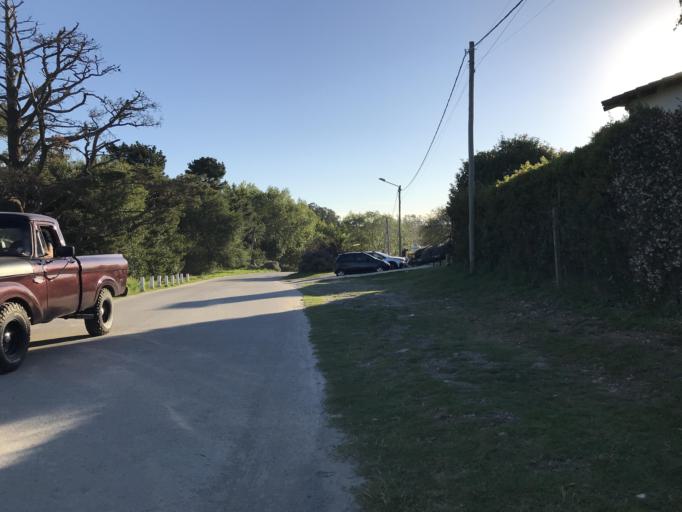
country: AR
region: Buenos Aires
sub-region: Partido de Tandil
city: Tandil
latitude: -37.3392
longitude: -59.1167
